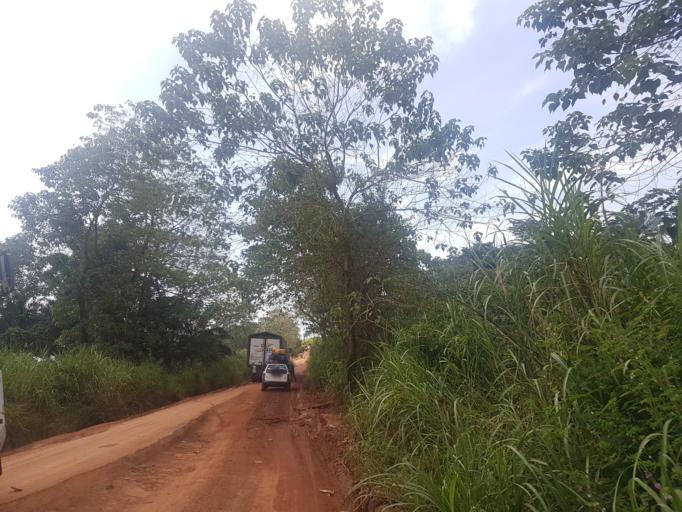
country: GN
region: Nzerekore
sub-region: Prefecture de Guekedou
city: Gueckedou
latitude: 8.7040
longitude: -10.1269
